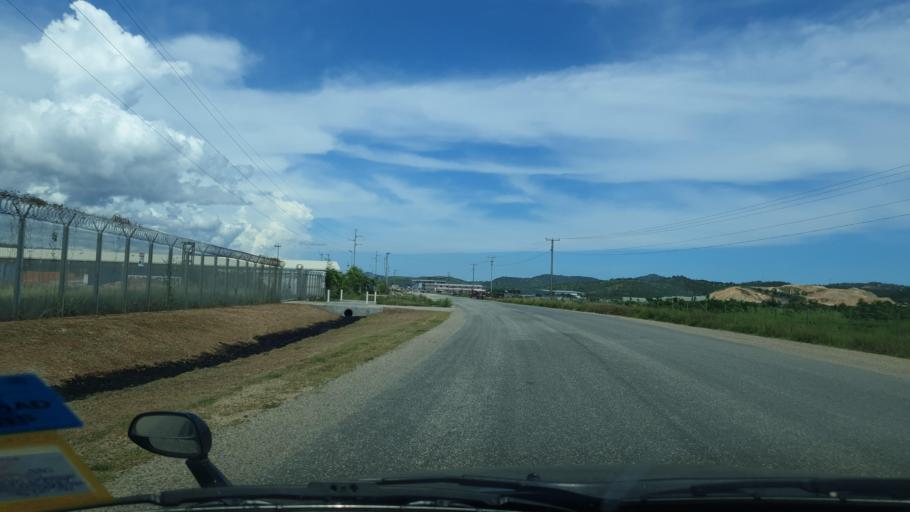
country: PG
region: National Capital
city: Port Moresby
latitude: -9.4155
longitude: 147.0732
